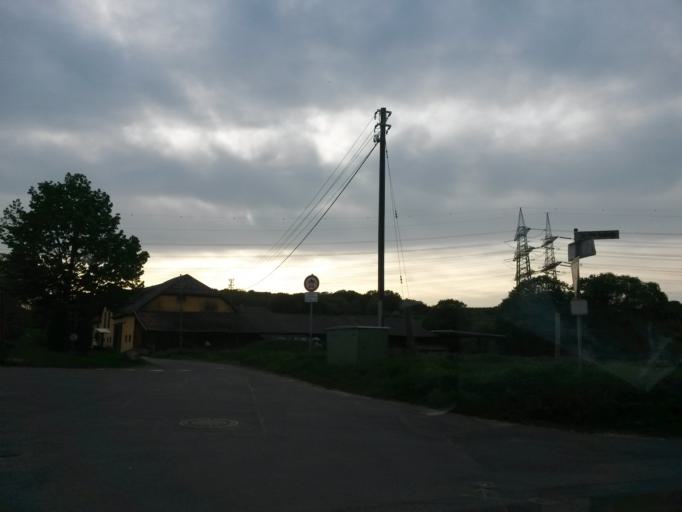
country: DE
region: North Rhine-Westphalia
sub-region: Regierungsbezirk Koln
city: Alfter
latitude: 50.7040
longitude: 7.0126
